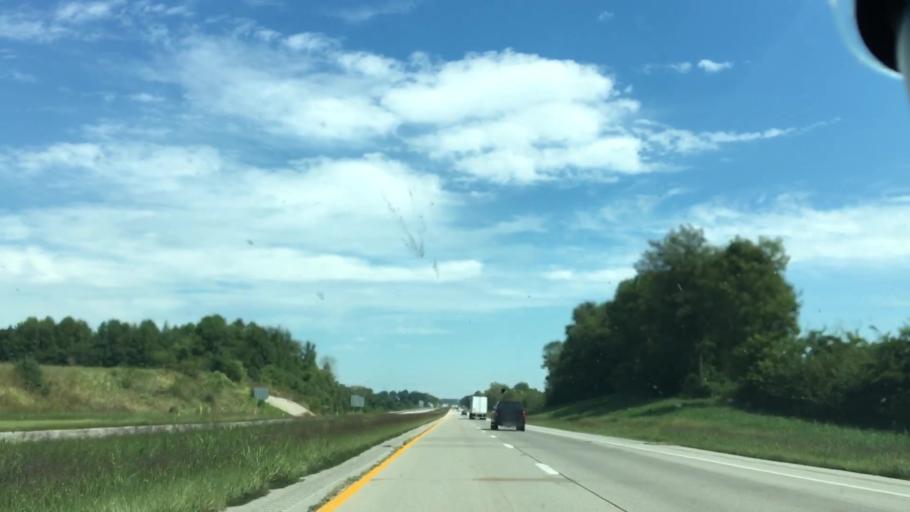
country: US
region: Kentucky
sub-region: Daviess County
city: Owensboro
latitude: 37.7569
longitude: -87.2581
